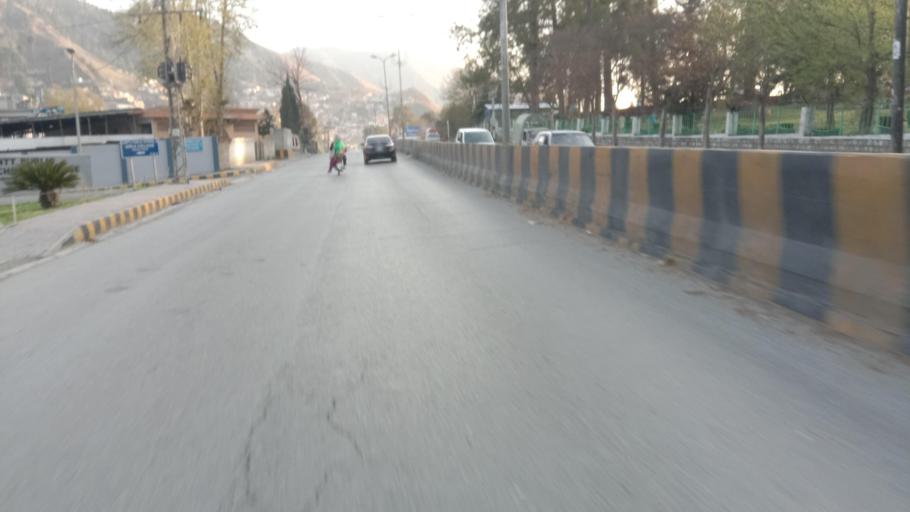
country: PK
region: Khyber Pakhtunkhwa
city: Abbottabad
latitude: 34.1500
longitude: 73.2168
